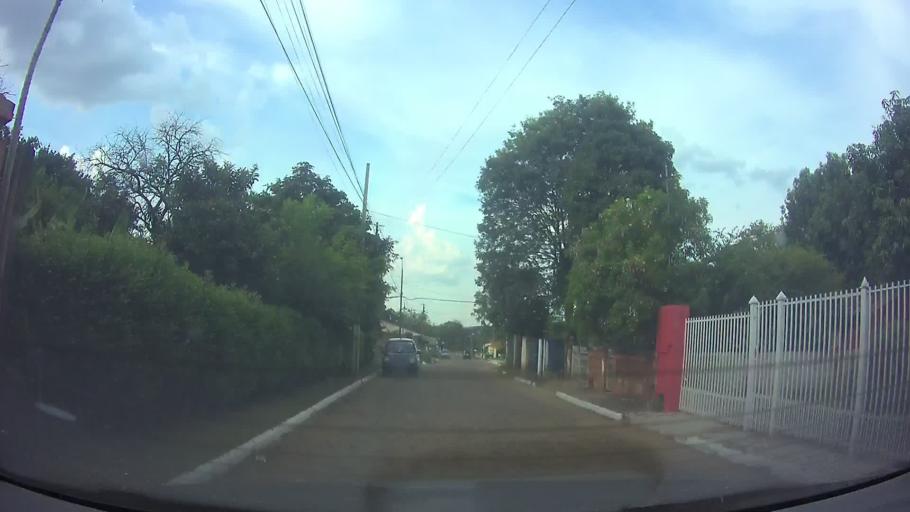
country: PY
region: Central
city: San Lorenzo
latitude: -25.2670
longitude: -57.4770
